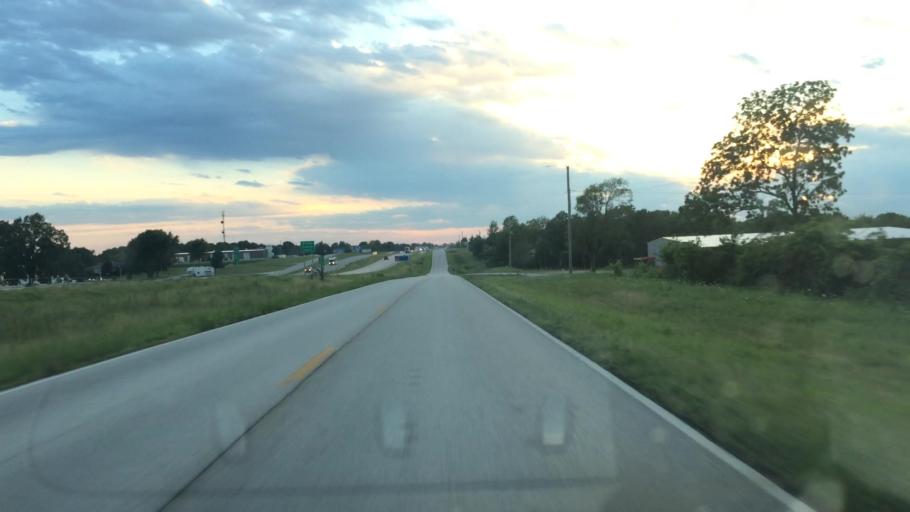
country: US
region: Missouri
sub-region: Greene County
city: Strafford
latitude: 37.2709
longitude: -93.0762
